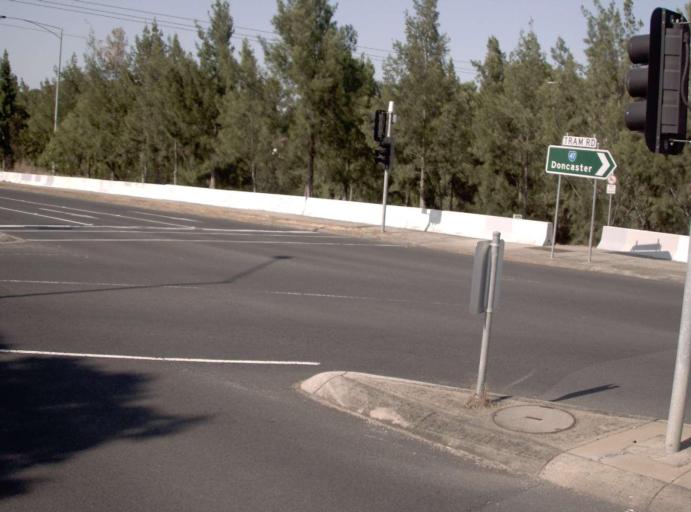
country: AU
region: Victoria
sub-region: Whitehorse
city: Box Hill North
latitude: -37.7975
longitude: 145.1270
